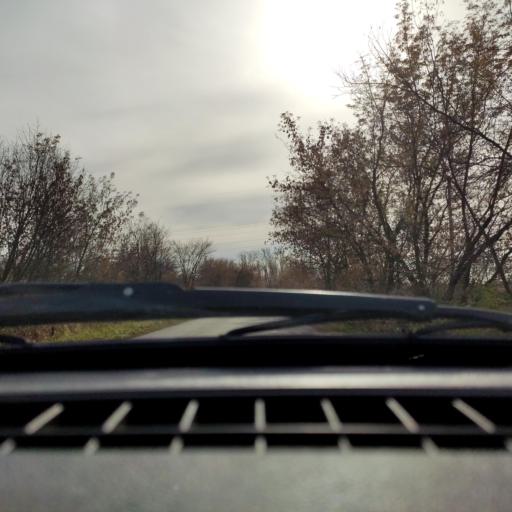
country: RU
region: Bashkortostan
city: Ufa
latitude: 54.7881
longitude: 56.1594
